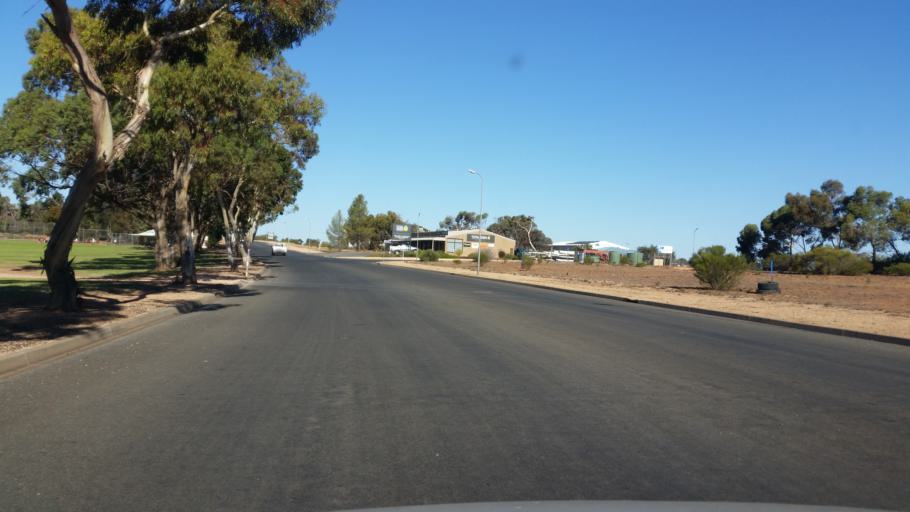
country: AU
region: South Australia
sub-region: Loxton Waikerie
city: Waikerie
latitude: -34.1884
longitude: 139.9788
